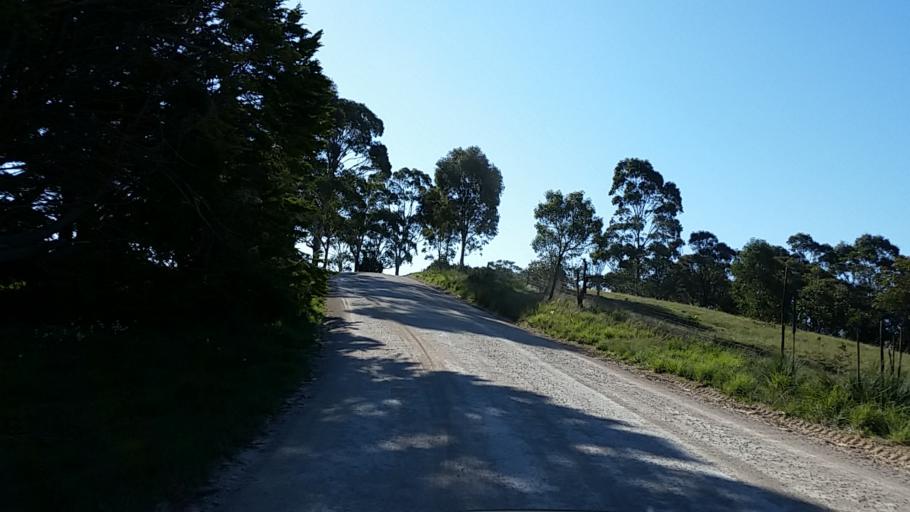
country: AU
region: South Australia
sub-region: Adelaide Hills
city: Lobethal
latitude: -34.8884
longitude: 138.8301
